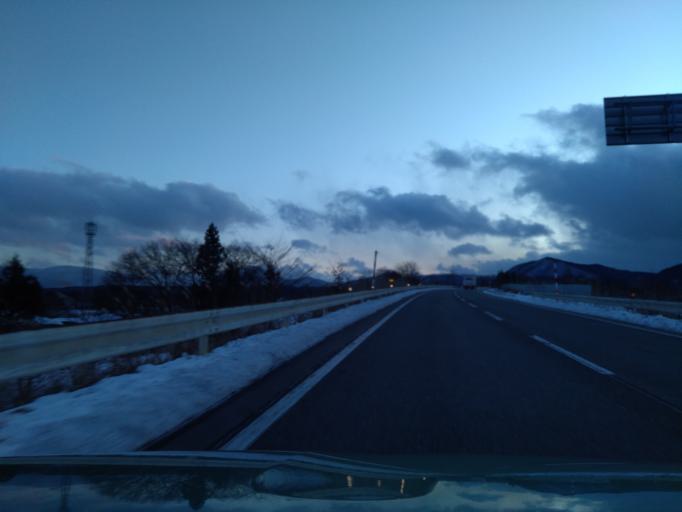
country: JP
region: Iwate
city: Shizukuishi
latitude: 39.6951
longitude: 140.9362
